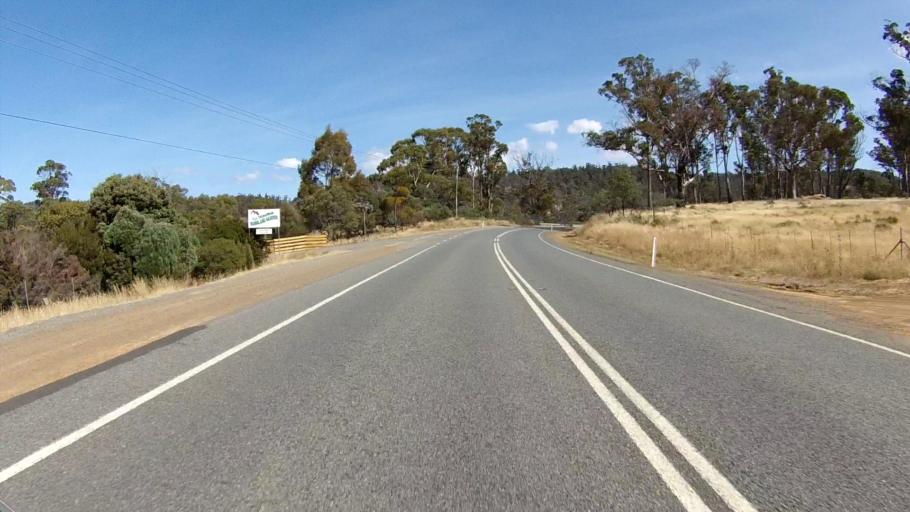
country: AU
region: Tasmania
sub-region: Sorell
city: Sorell
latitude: -42.6078
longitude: 147.6710
